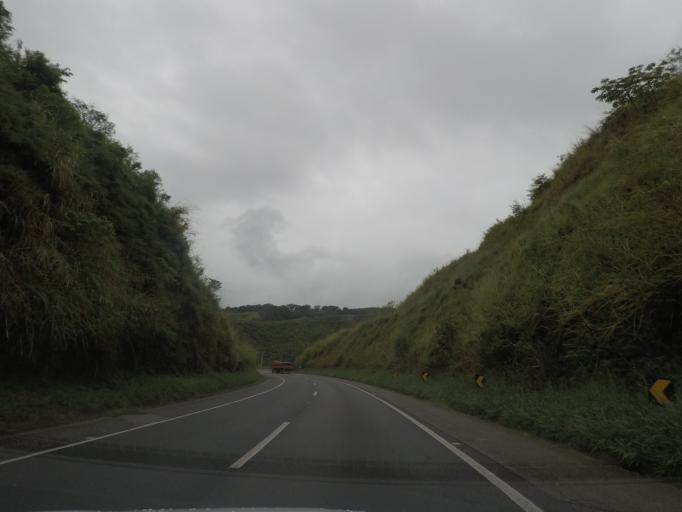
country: BR
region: Sao Paulo
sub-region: Cajati
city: Cajati
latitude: -24.8312
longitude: -48.2104
